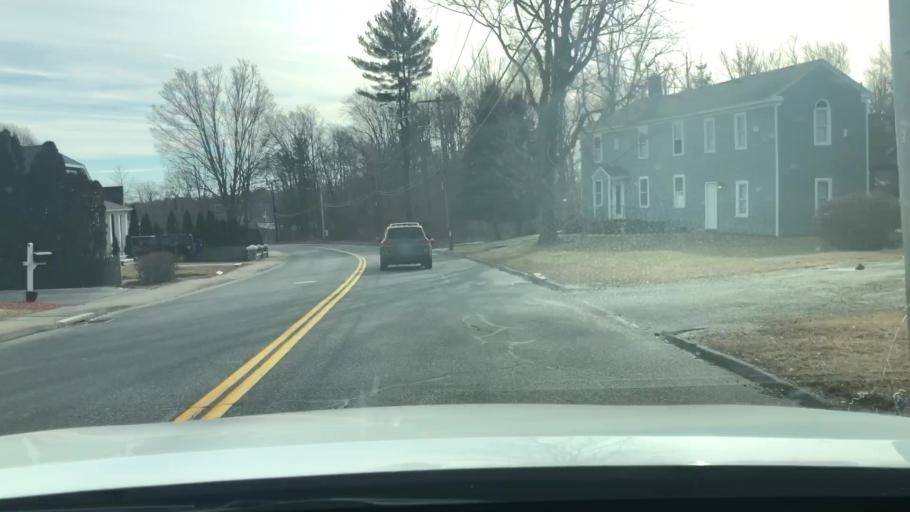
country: US
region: Massachusetts
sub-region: Worcester County
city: Hopedale
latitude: 42.1421
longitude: -71.5368
